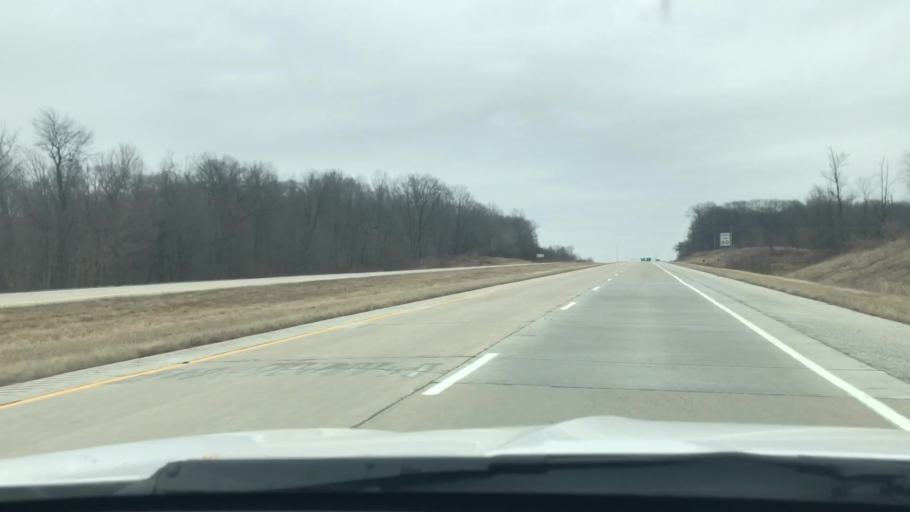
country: US
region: Indiana
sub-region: Miami County
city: Peru
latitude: 40.7704
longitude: -86.1472
